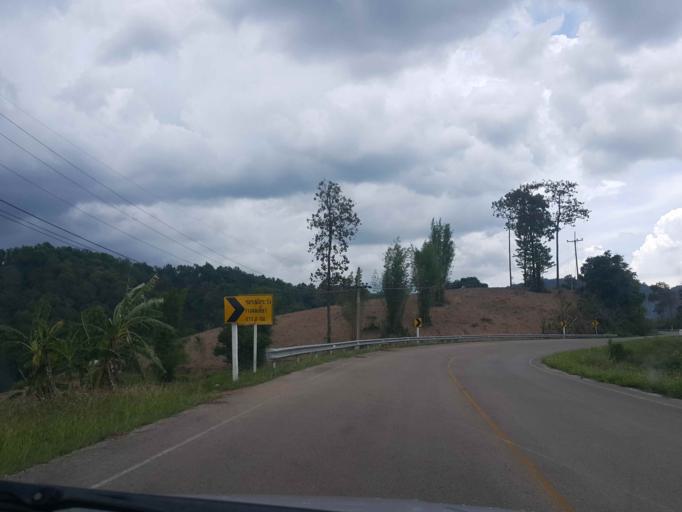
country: TH
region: Lampang
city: Ngao
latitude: 18.9346
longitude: 100.0868
